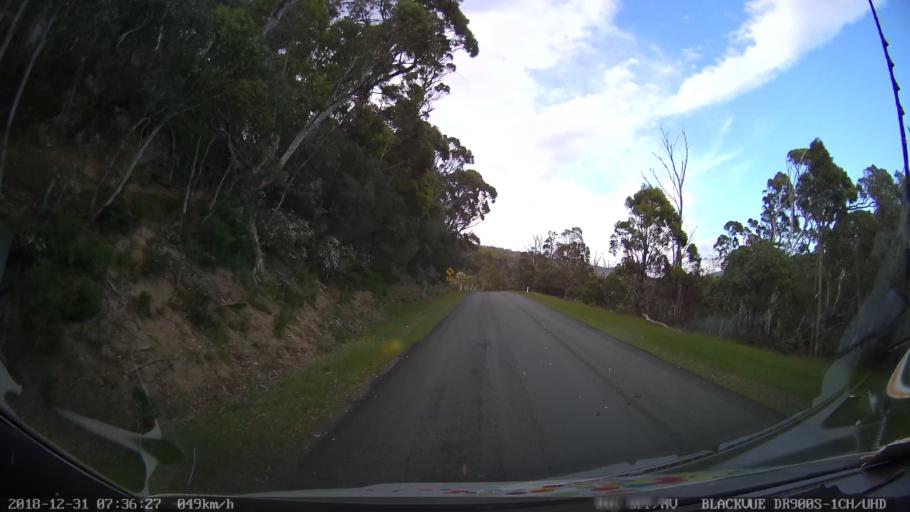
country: AU
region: New South Wales
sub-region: Snowy River
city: Jindabyne
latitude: -36.3410
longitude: 148.4427
